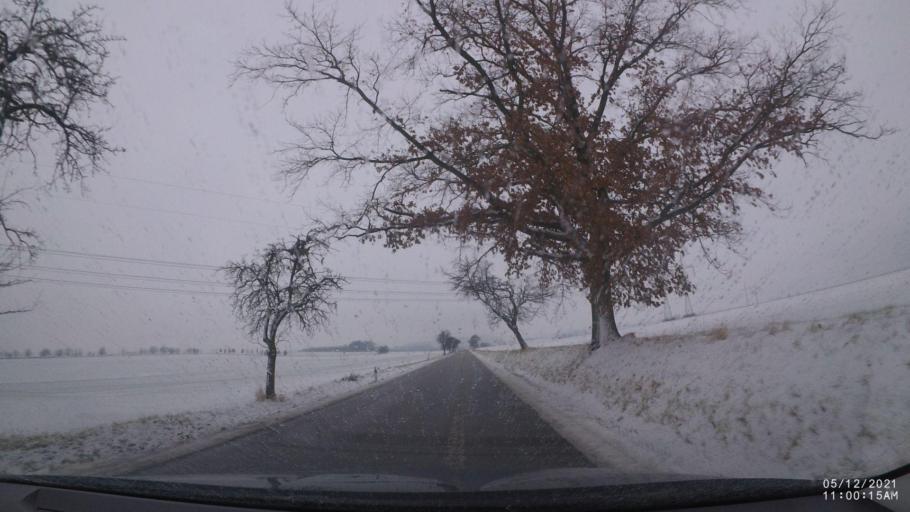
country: CZ
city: Solnice
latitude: 50.1667
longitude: 16.2243
